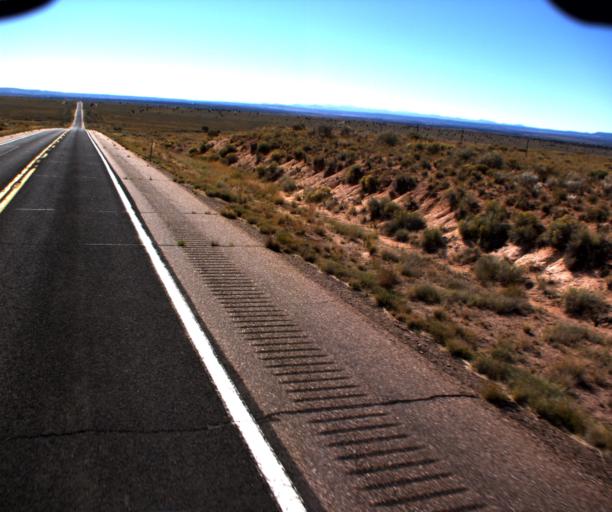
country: US
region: Arizona
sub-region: Navajo County
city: Snowflake
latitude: 34.7024
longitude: -109.7551
